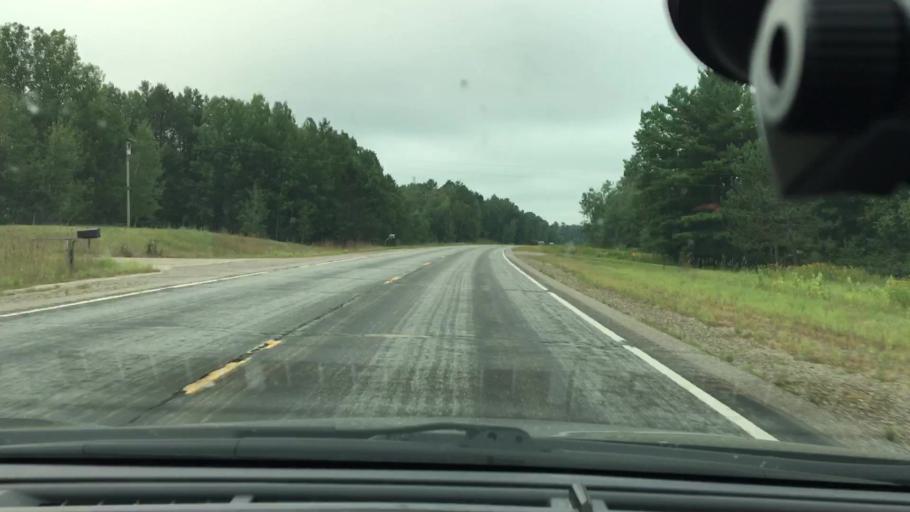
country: US
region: Minnesota
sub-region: Crow Wing County
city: Cross Lake
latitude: 46.6705
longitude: -93.9517
